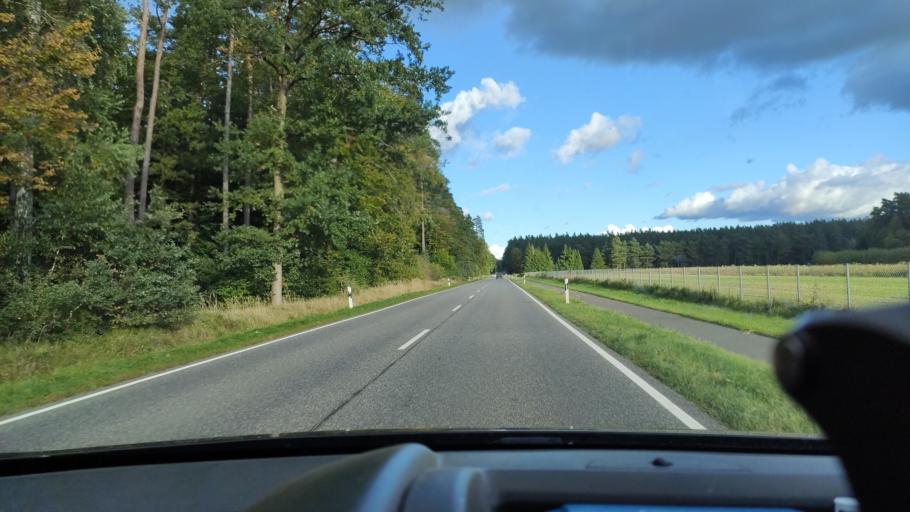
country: DE
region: Mecklenburg-Vorpommern
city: Muhl Rosin
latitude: 53.7720
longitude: 12.3004
